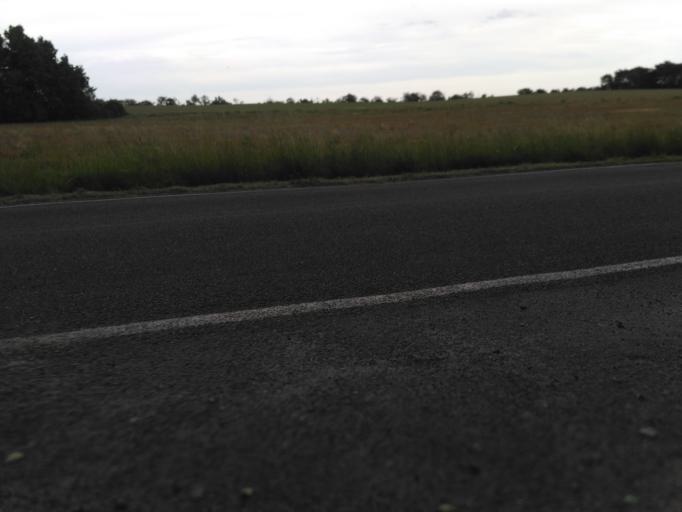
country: DE
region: Brandenburg
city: Hohenleipisch
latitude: 51.4888
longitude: 13.5247
